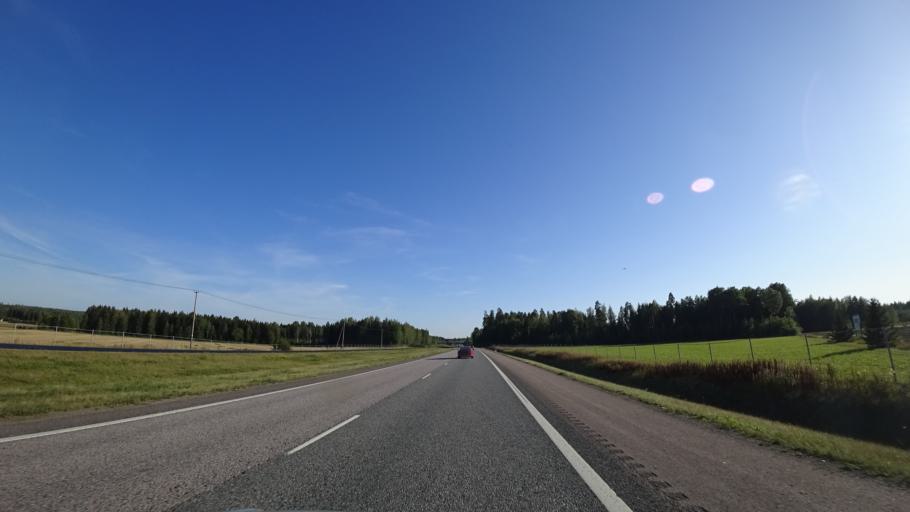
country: FI
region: Uusimaa
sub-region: Helsinki
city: Nurmijaervi
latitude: 60.4790
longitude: 24.8487
